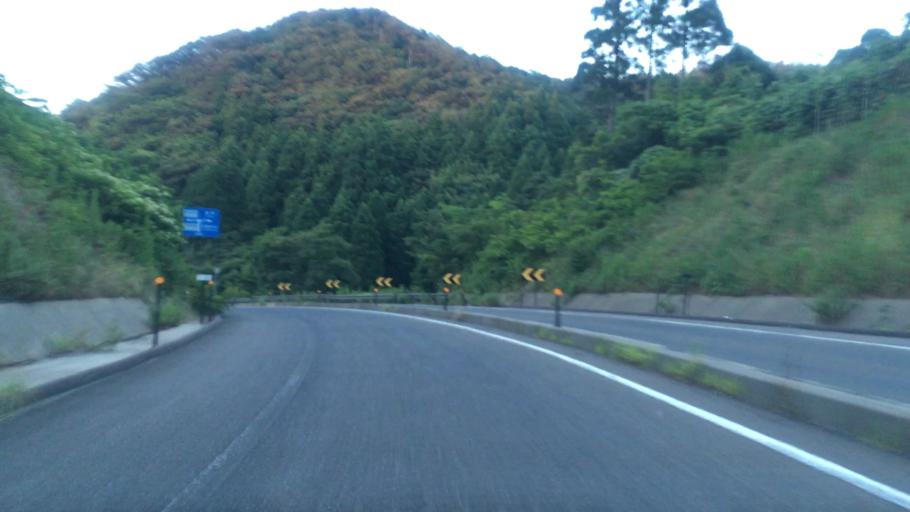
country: JP
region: Tottori
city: Tottori
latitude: 35.6121
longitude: 134.3935
